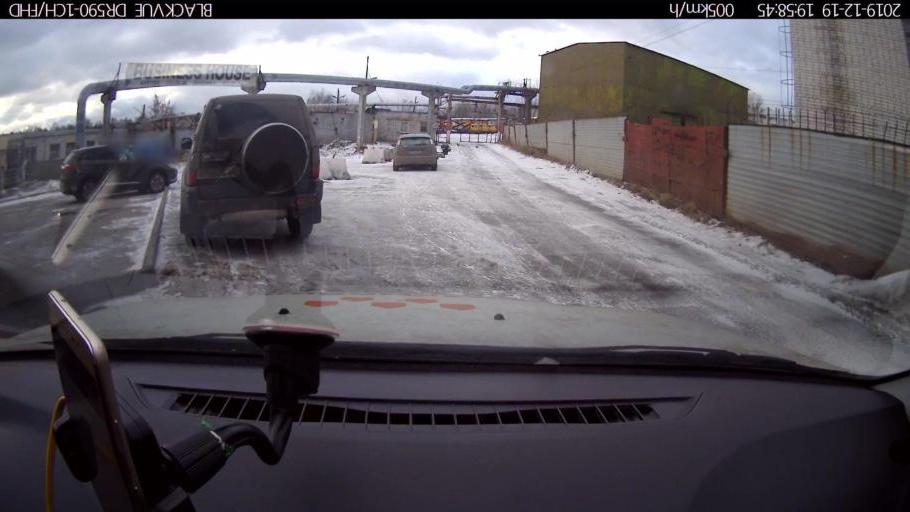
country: RU
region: Nizjnij Novgorod
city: Nizhniy Novgorod
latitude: 56.3026
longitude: 44.0212
